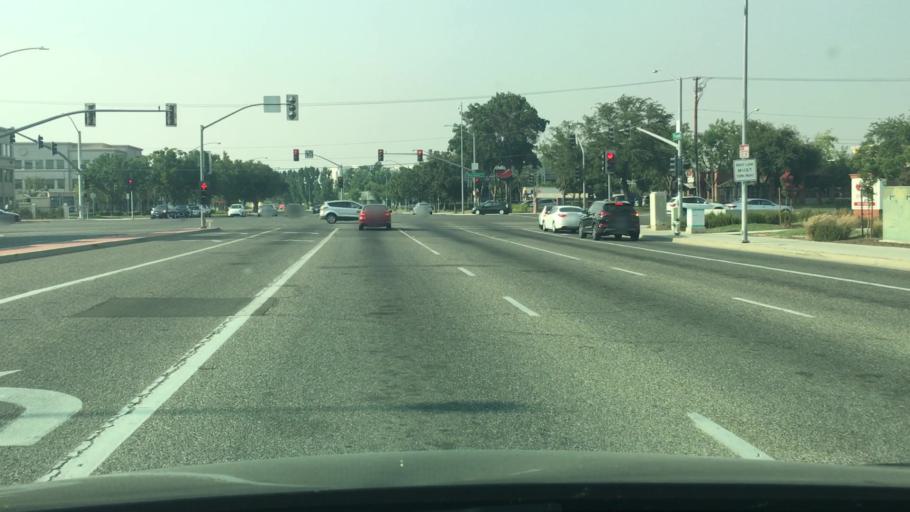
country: US
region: California
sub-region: Fresno County
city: Clovis
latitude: 36.8368
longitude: -119.7812
